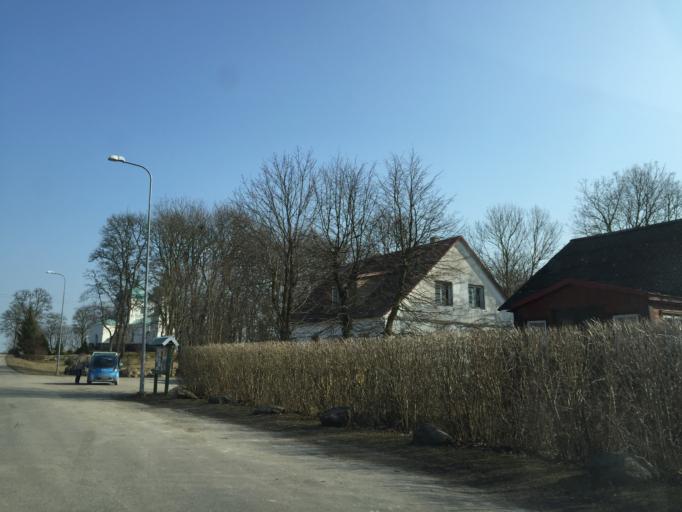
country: EE
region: Saare
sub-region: Orissaare vald
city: Orissaare
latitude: 58.5040
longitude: 23.1176
